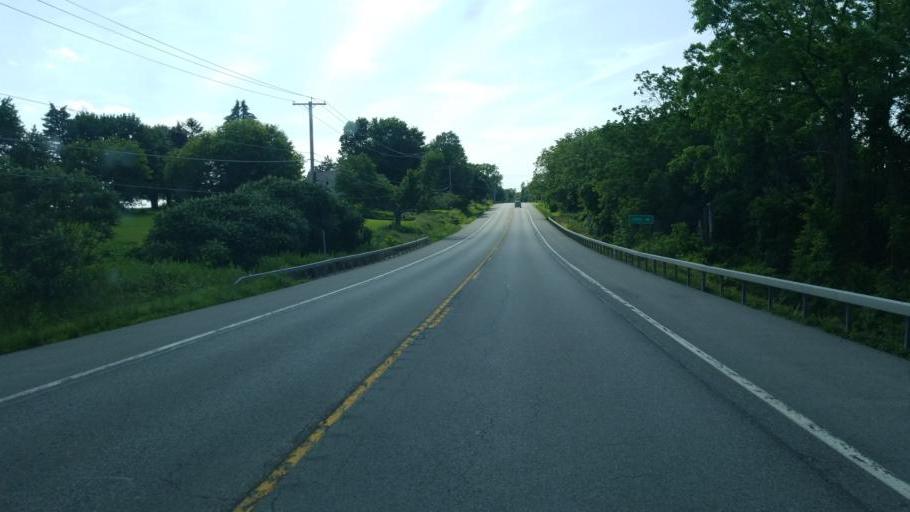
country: US
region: New York
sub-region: Ontario County
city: Holcomb
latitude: 42.9020
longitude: -77.4937
